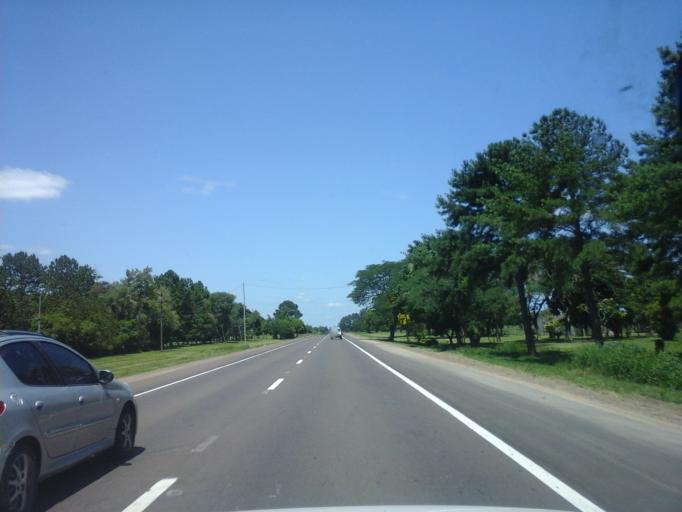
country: AR
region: Corrientes
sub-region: Departamento de Itati
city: Itati
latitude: -27.3671
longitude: -58.3574
